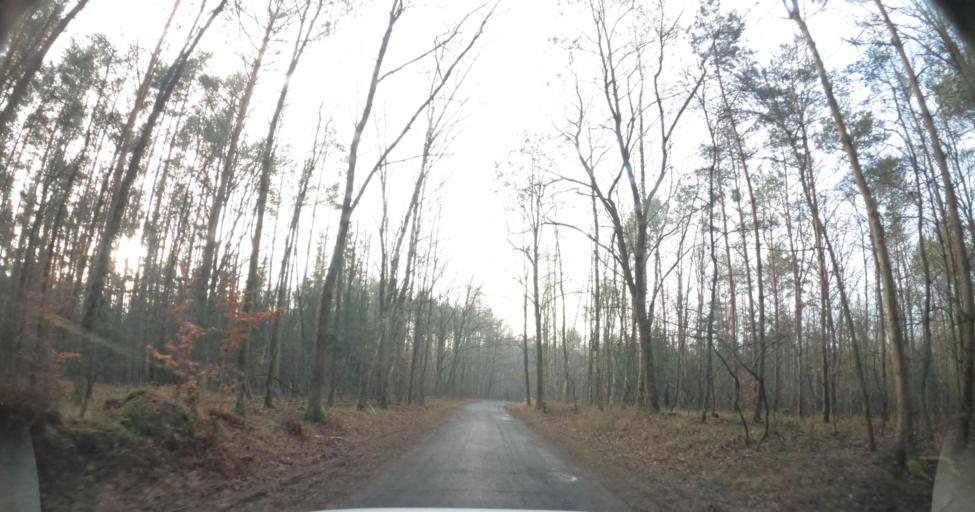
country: PL
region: West Pomeranian Voivodeship
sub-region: Powiat mysliborski
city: Boleszkowice
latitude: 52.7132
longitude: 14.5566
